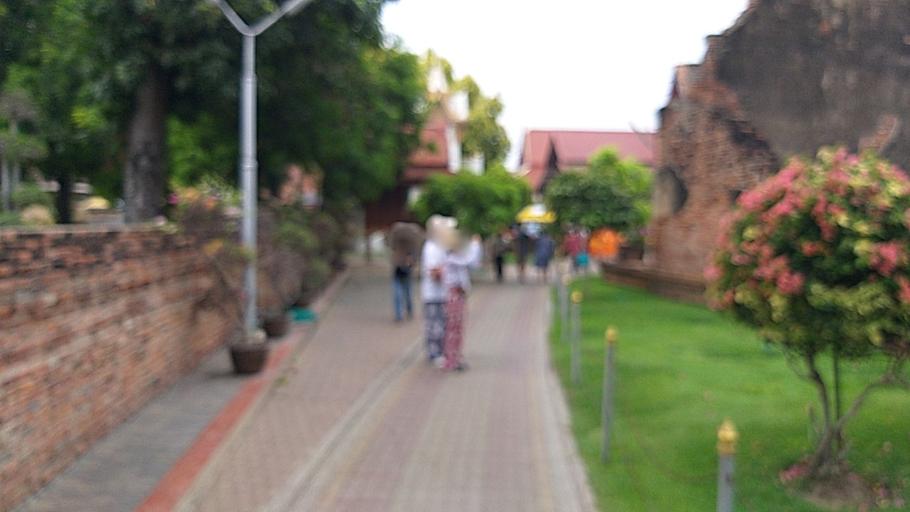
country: TH
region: Phra Nakhon Si Ayutthaya
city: Phra Nakhon Si Ayutthaya
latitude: 14.3461
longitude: 100.5932
